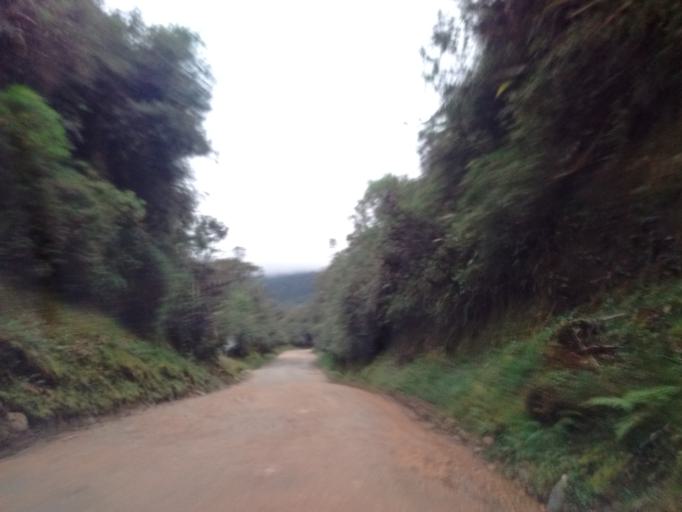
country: CO
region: Huila
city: Isnos
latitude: 2.1288
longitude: -76.3799
